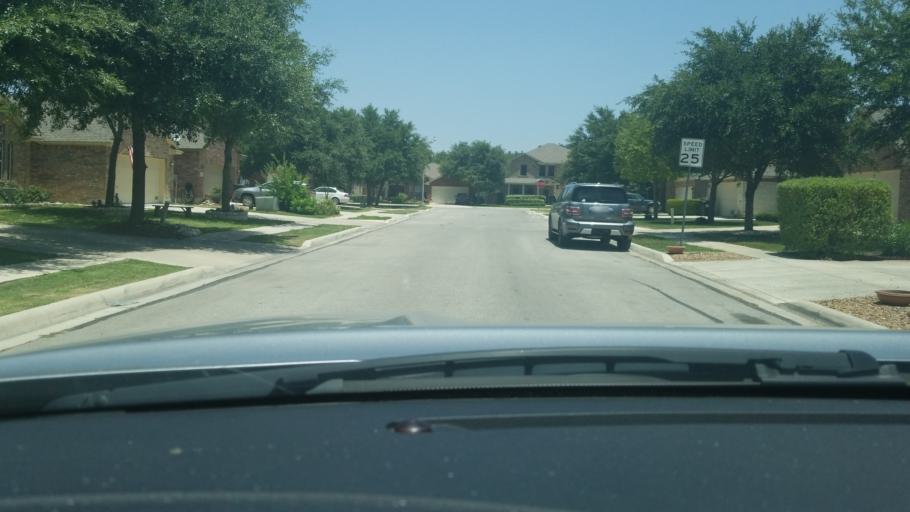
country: US
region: Texas
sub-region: Guadalupe County
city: Cibolo
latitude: 29.5756
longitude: -98.2268
